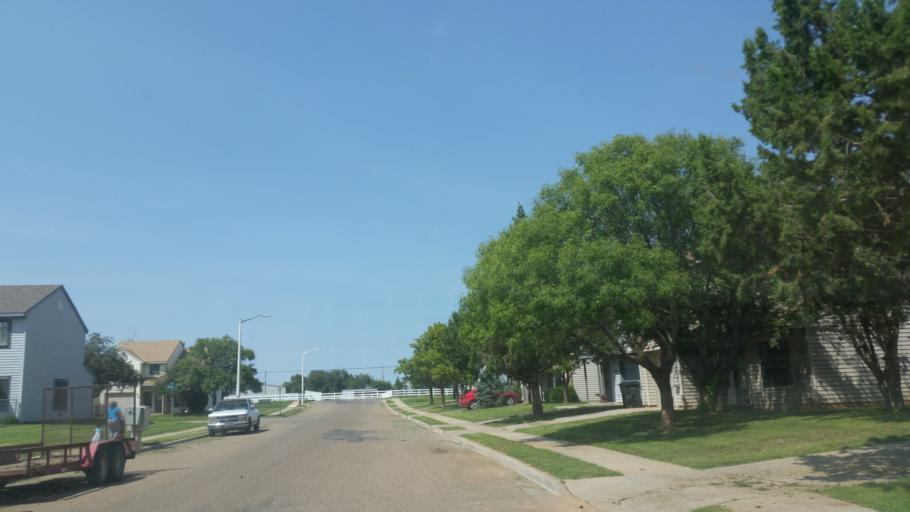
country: US
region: New Mexico
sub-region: Curry County
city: Clovis
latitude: 34.4473
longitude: -103.1733
